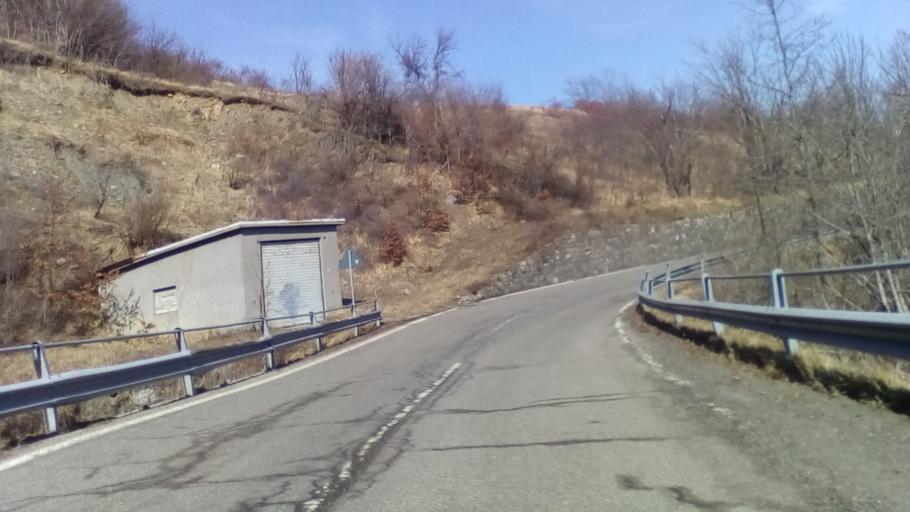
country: IT
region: Emilia-Romagna
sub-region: Provincia di Modena
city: Riolunato
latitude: 44.2337
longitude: 10.6252
